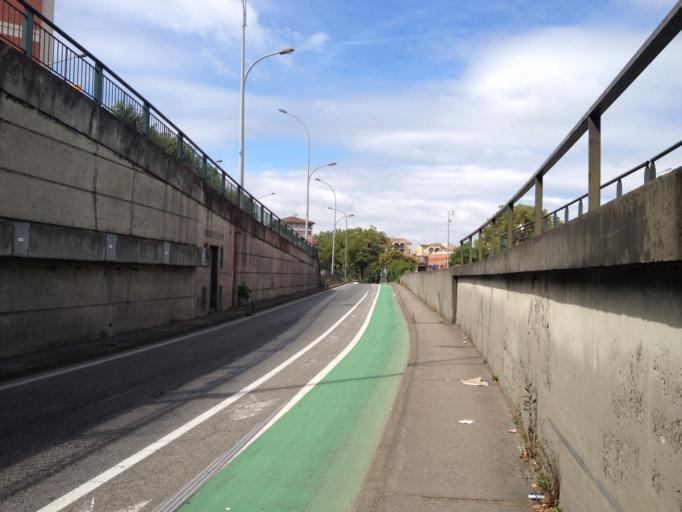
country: FR
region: Midi-Pyrenees
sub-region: Departement de la Haute-Garonne
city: Toulouse
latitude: 43.6160
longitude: 1.4370
